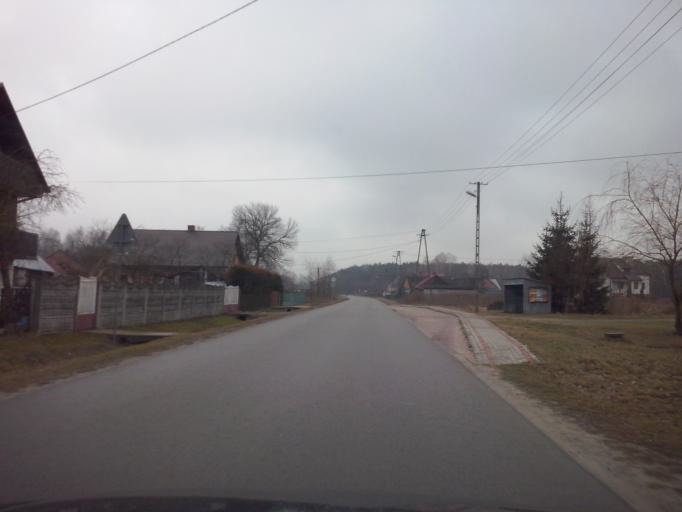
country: PL
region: Subcarpathian Voivodeship
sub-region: Powiat nizanski
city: Bieliny
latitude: 50.4430
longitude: 22.3028
